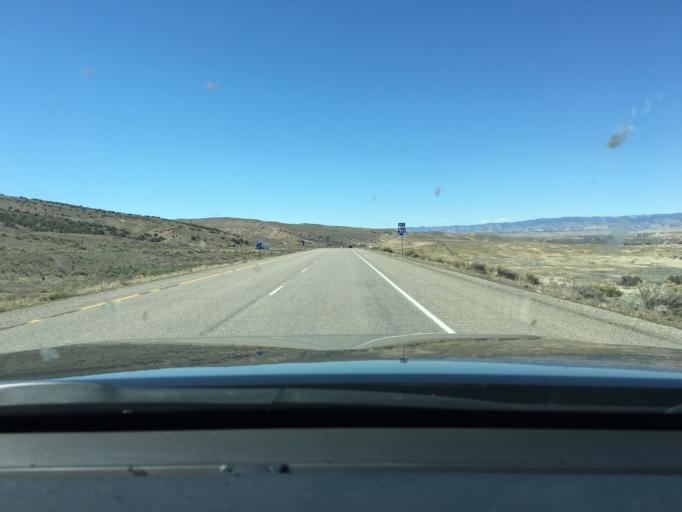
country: US
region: Colorado
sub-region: Mesa County
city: Loma
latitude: 39.2173
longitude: -108.8745
